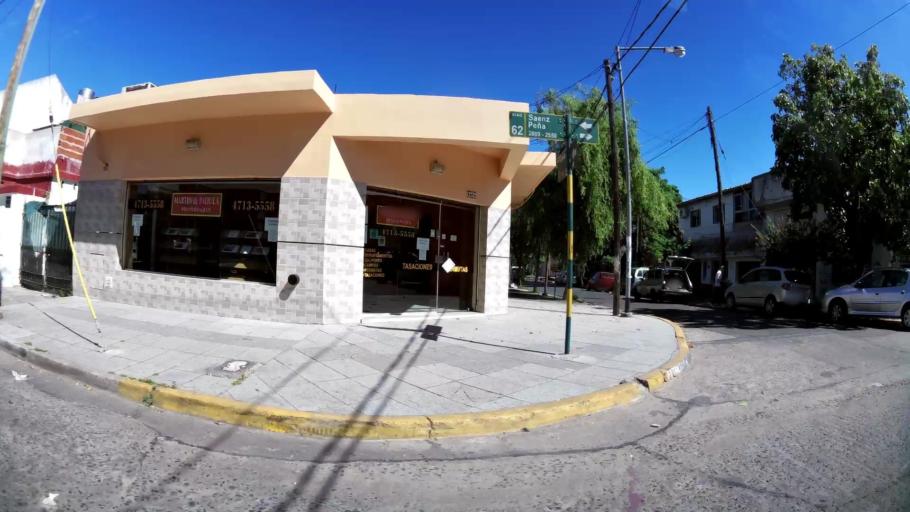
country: AR
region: Buenos Aires
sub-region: Partido de General San Martin
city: General San Martin
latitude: -34.5656
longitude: -58.5324
